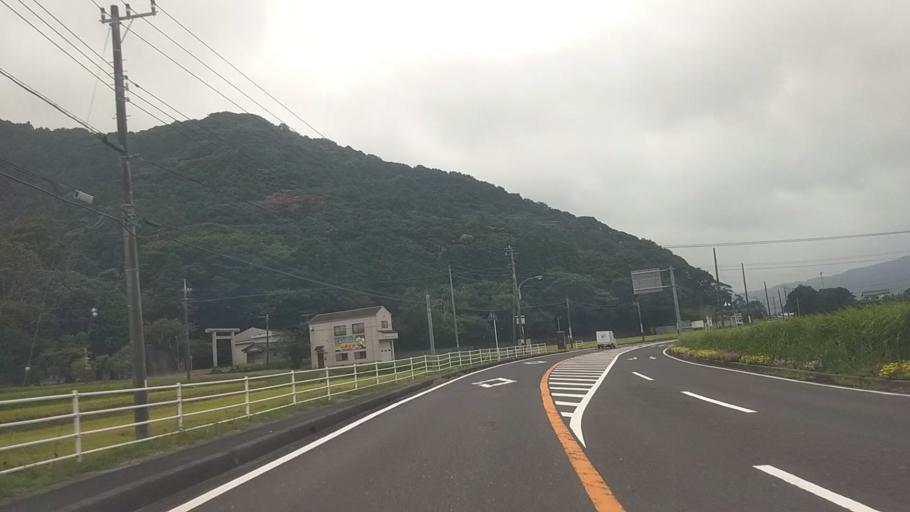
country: JP
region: Chiba
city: Kawaguchi
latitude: 35.1324
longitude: 140.0788
